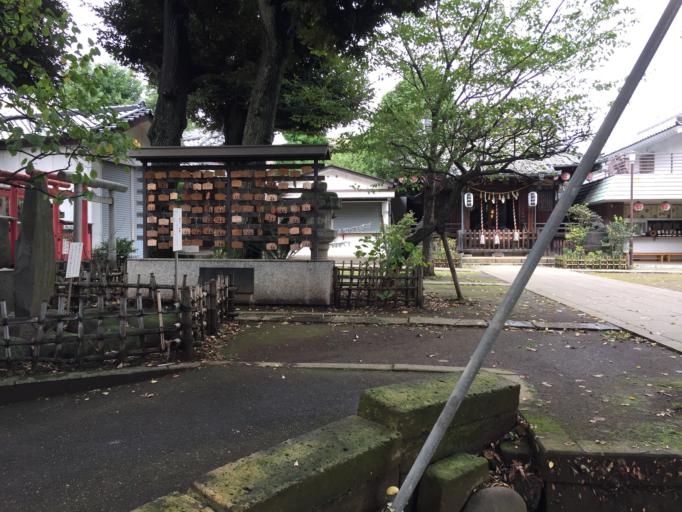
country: JP
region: Tokyo
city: Tokyo
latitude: 35.7151
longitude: 139.6664
